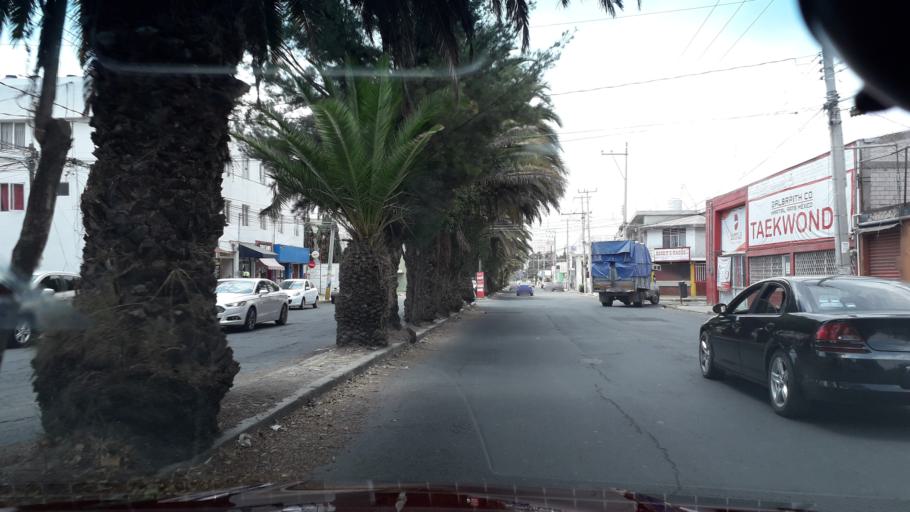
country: MX
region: Puebla
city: Puebla
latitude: 19.0058
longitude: -98.2350
